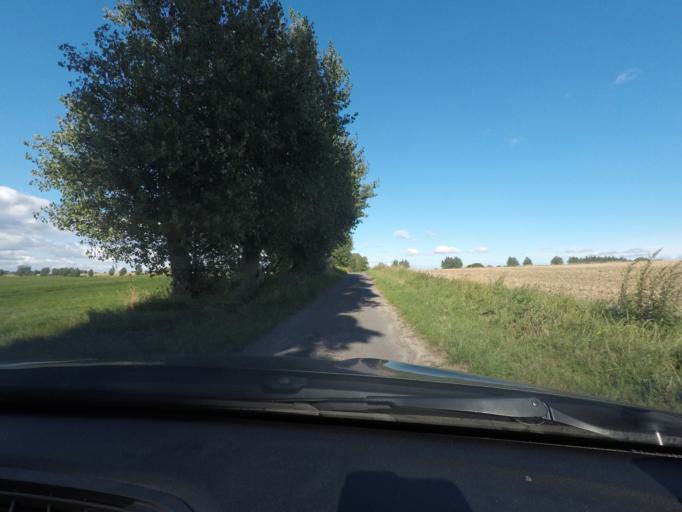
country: DK
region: Zealand
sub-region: Guldborgsund Kommune
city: Sakskobing
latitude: 54.9559
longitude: 11.5360
